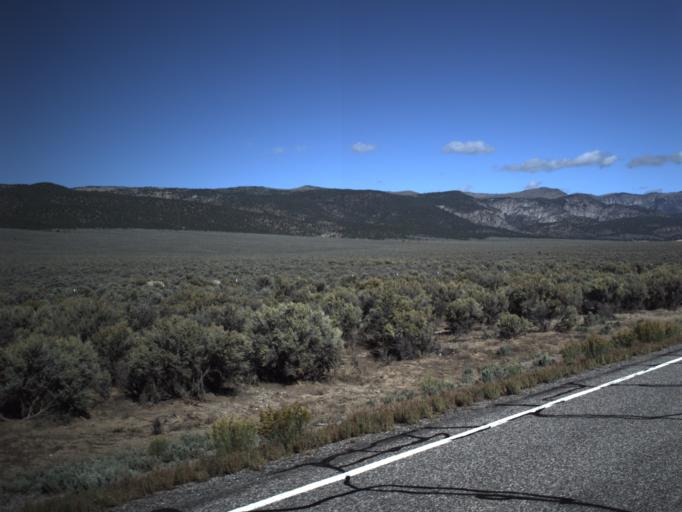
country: US
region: Utah
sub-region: Piute County
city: Junction
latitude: 38.2508
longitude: -111.9869
